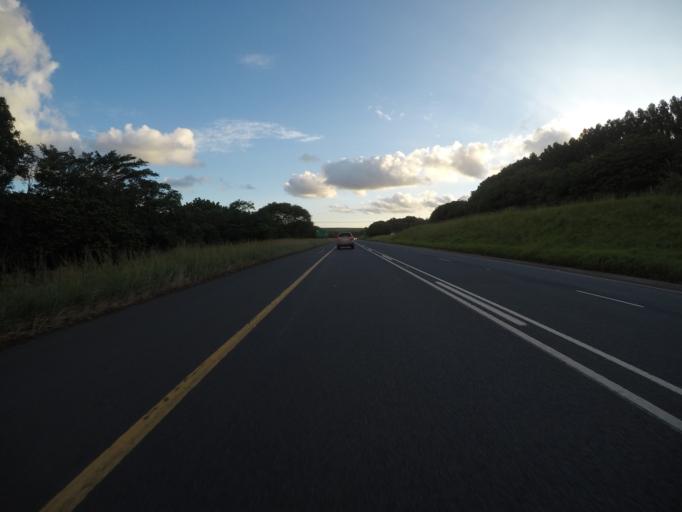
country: ZA
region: KwaZulu-Natal
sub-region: uThungulu District Municipality
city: Richards Bay
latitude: -28.6854
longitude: 32.0399
